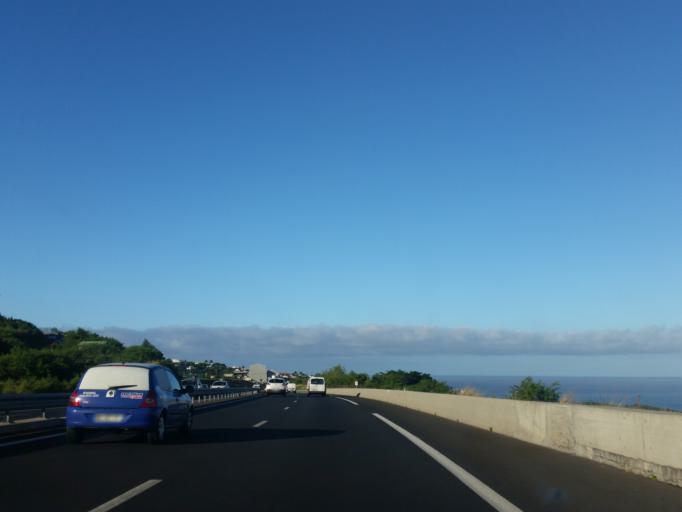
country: RE
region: Reunion
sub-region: Reunion
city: Saint-Leu
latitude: -21.1915
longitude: 55.2963
